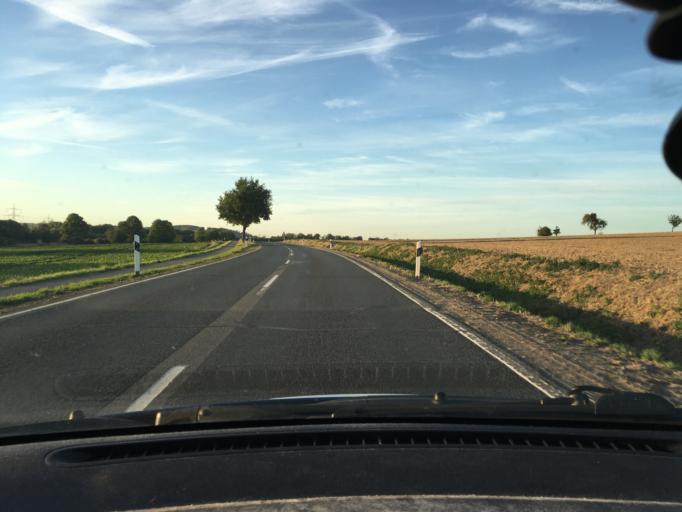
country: DE
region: Lower Saxony
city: Lauenau
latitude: 52.2824
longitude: 9.3640
